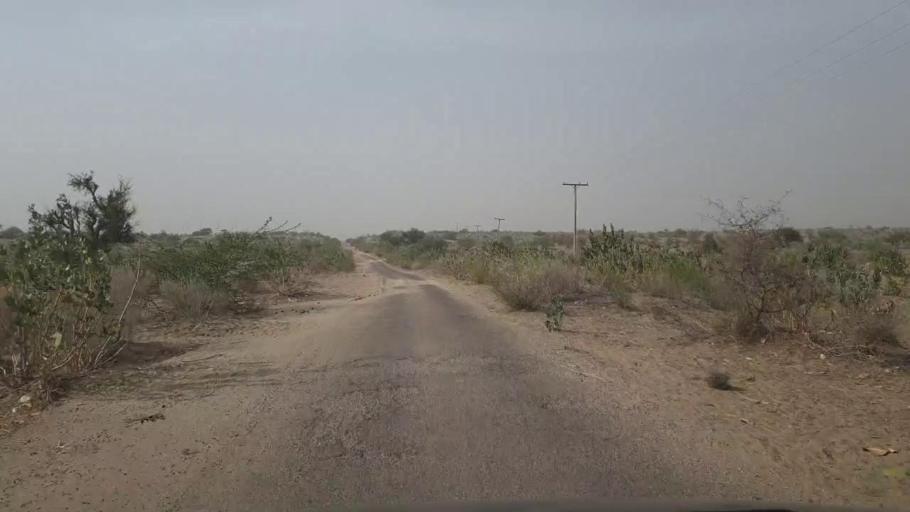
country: PK
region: Sindh
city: Chor
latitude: 25.5932
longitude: 69.9471
